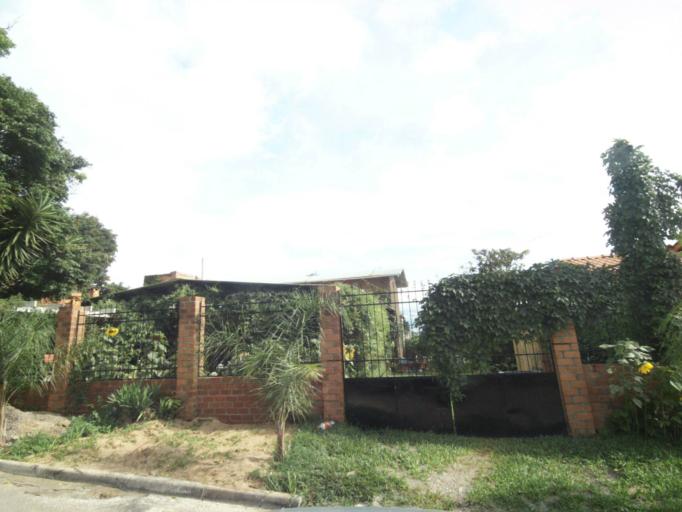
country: BR
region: Rio Grande do Sul
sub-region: Lagoa Vermelha
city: Lagoa Vermelha
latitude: -28.2110
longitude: -51.5315
